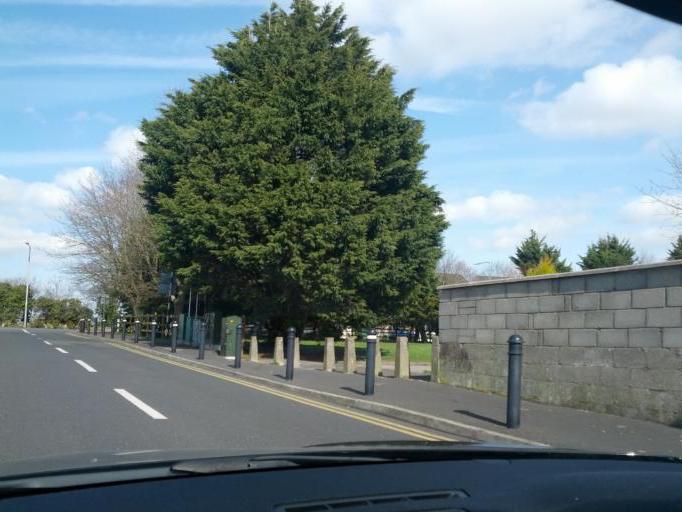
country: IE
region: Leinster
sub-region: Kildare
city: Leixlip
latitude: 53.3689
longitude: -6.5071
